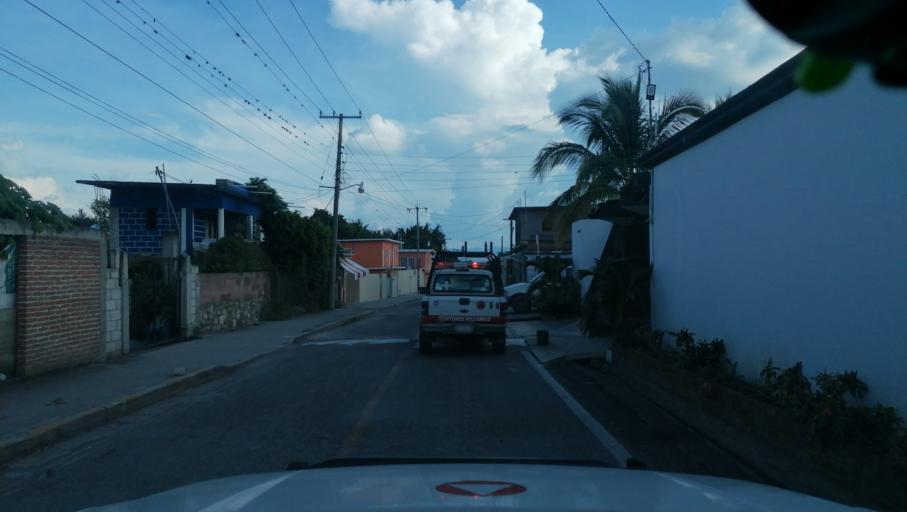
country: MX
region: Morelos
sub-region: Ayala
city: Abelardo L. Rodriguez
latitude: 18.7213
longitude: -98.9921
